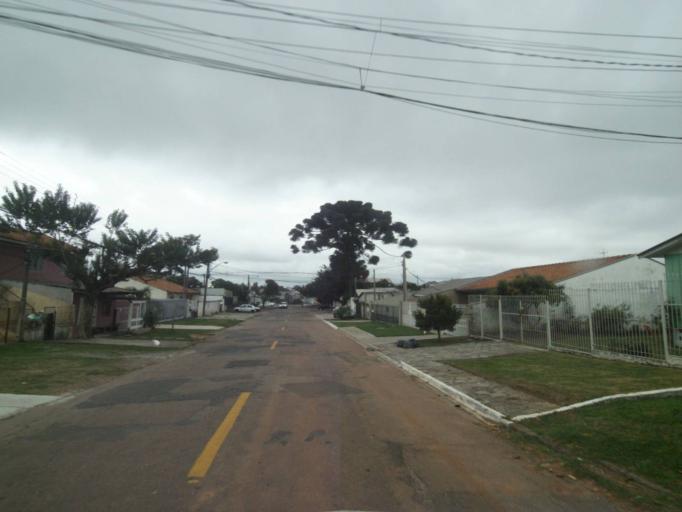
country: BR
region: Parana
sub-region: Sao Jose Dos Pinhais
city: Sao Jose dos Pinhais
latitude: -25.5404
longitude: -49.2836
